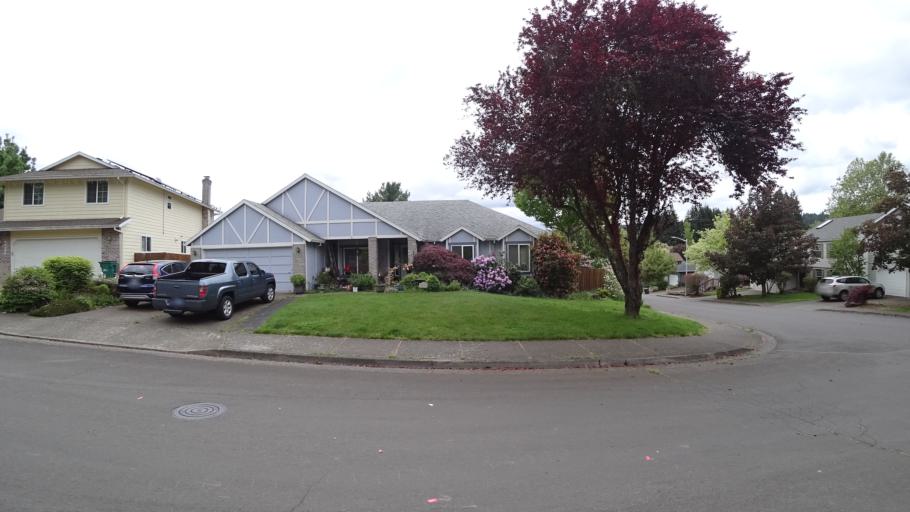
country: US
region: Oregon
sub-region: Washington County
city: Aloha
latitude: 45.4681
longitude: -122.8472
